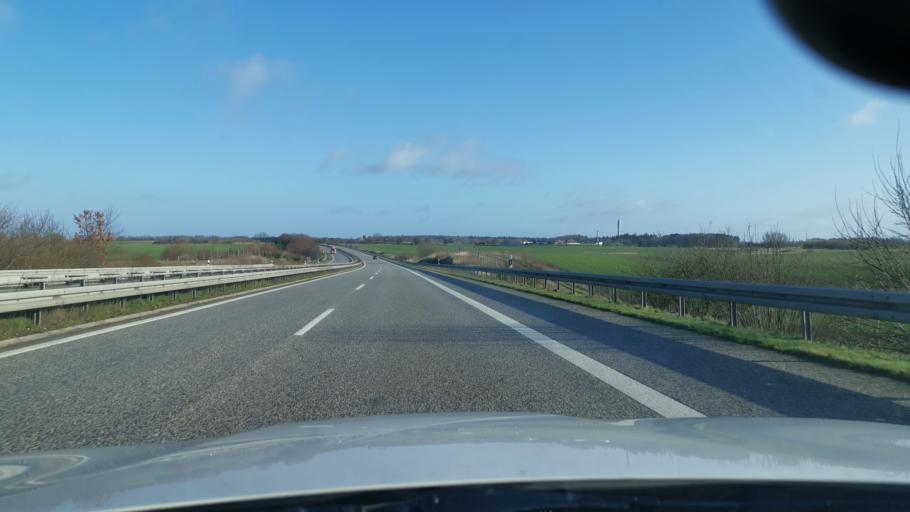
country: DE
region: Mecklenburg-Vorpommern
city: Kritzmow
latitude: 54.0577
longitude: 12.0407
